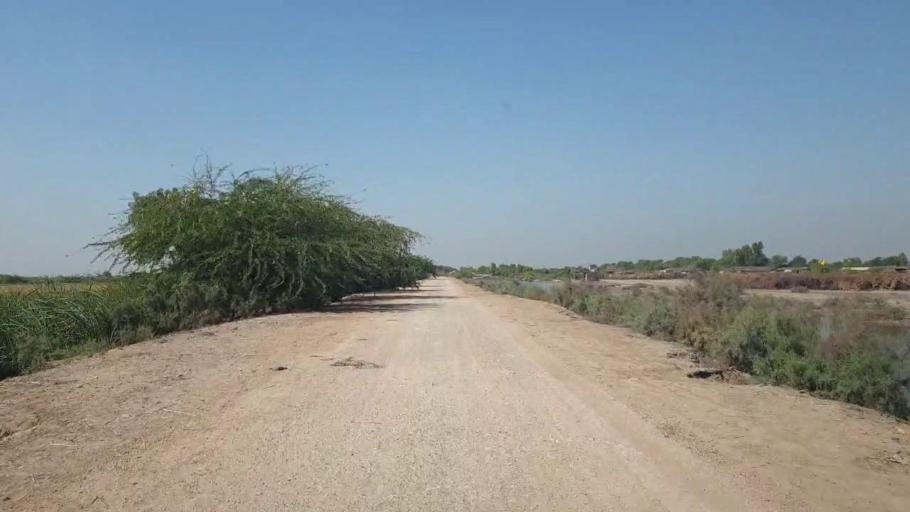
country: PK
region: Sindh
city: Talhar
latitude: 24.8288
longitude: 68.7835
